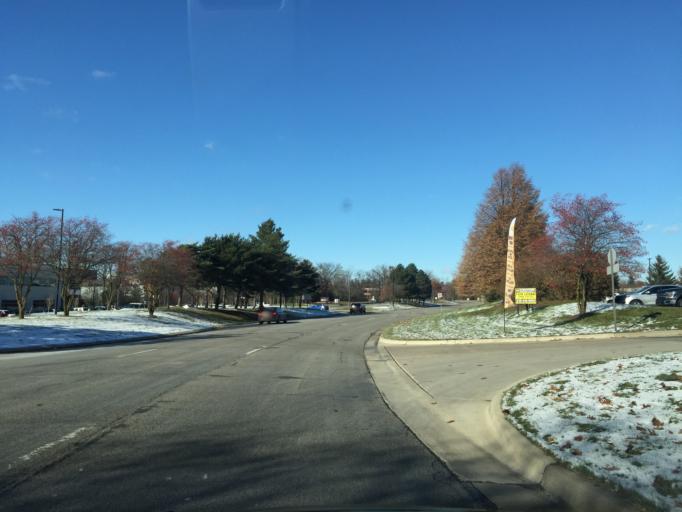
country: US
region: Michigan
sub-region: Oakland County
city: Auburn Hills
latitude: 42.6654
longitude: -83.2280
